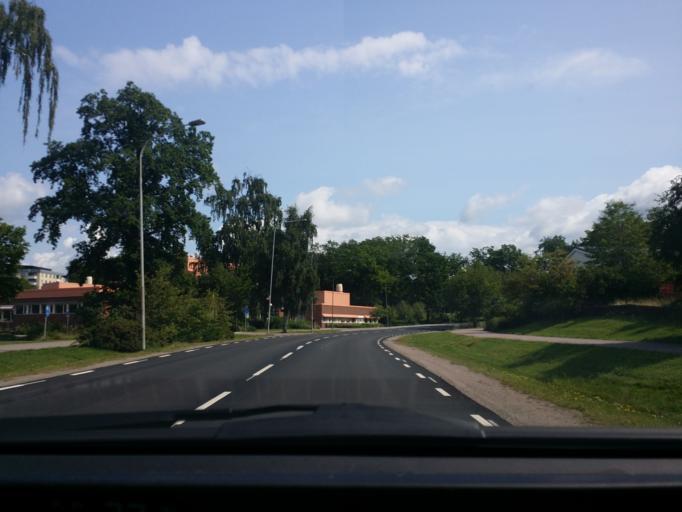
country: SE
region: Vaestmanland
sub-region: Vasteras
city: Vasteras
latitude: 59.6062
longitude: 16.5835
